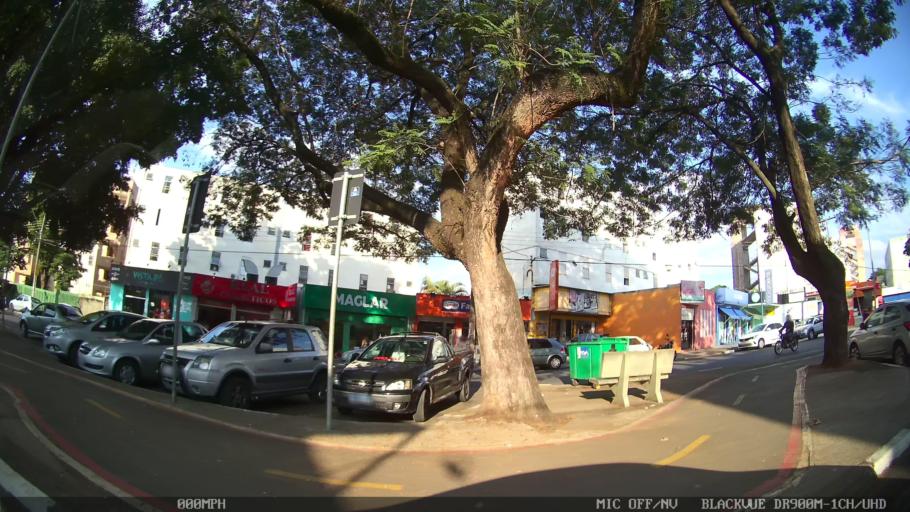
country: BR
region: Sao Paulo
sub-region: Hortolandia
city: Hortolandia
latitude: -22.8600
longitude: -47.1521
